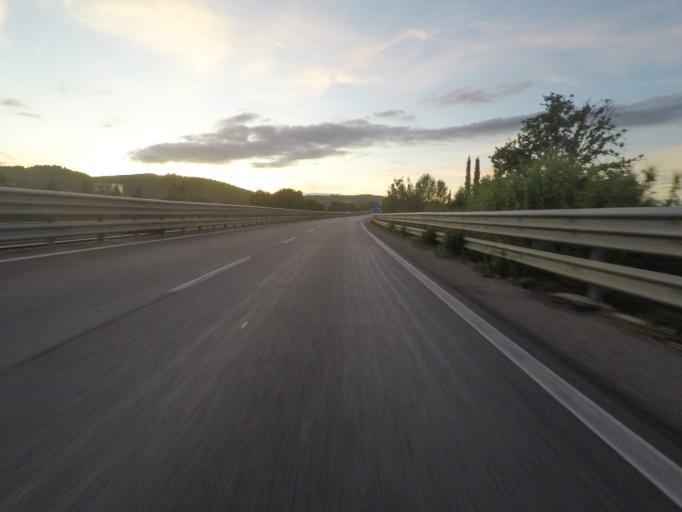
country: IT
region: Tuscany
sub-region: Provincia di Siena
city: Sinalunga
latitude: 43.2229
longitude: 11.7506
